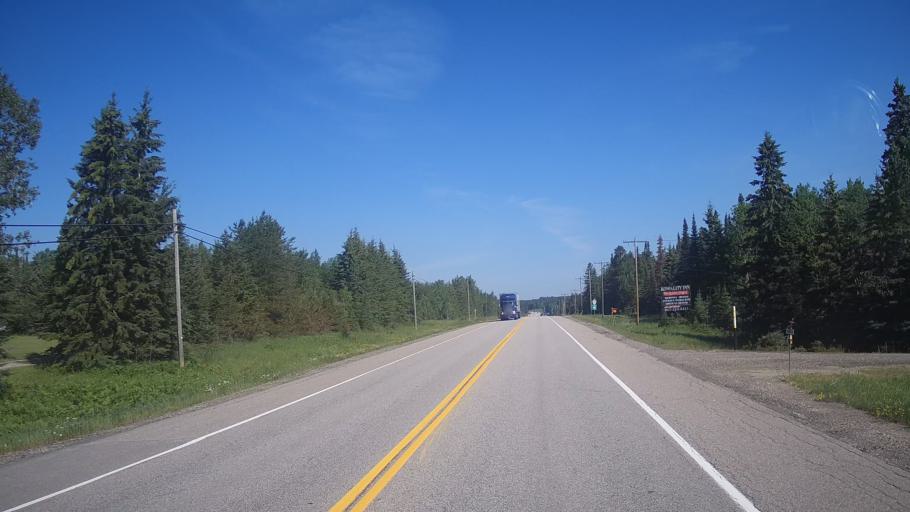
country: CA
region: Ontario
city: Dryden
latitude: 49.7719
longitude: -92.6911
